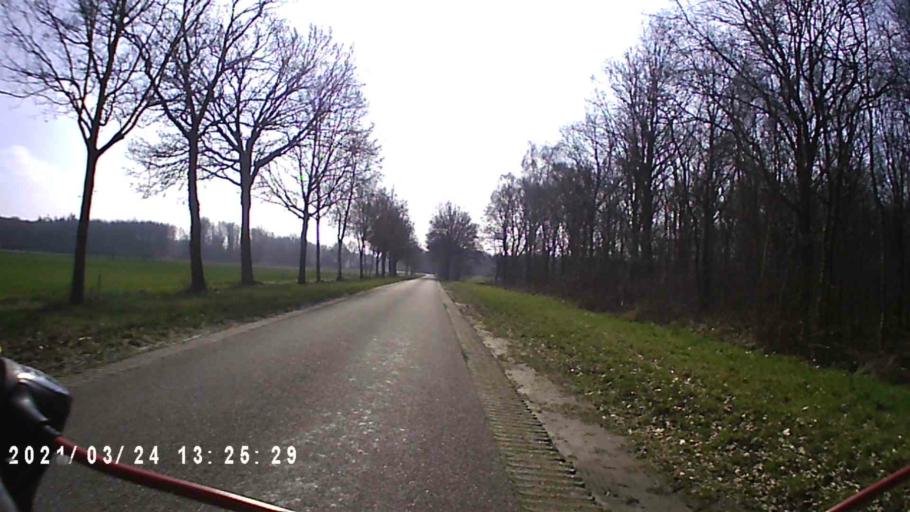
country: NL
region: Groningen
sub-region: Gemeente Grootegast
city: Grootegast
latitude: 53.0934
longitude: 6.2787
